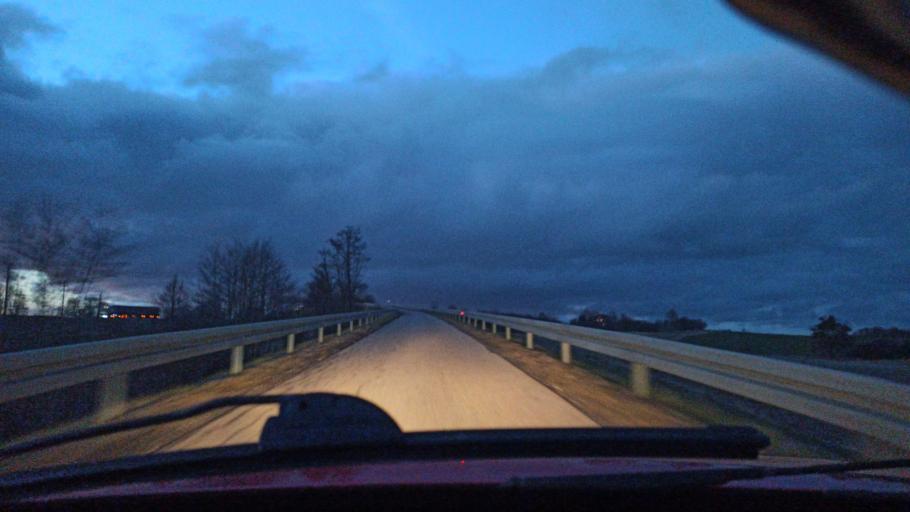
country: PL
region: Warmian-Masurian Voivodeship
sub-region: Powiat elblaski
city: Gronowo Gorne
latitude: 54.1703
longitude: 19.5357
